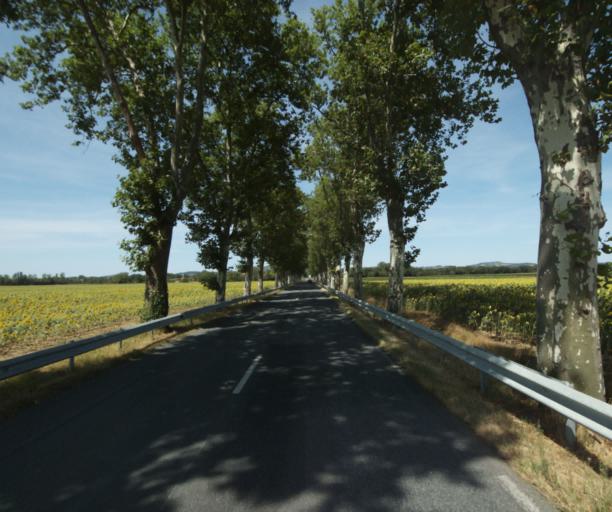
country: FR
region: Midi-Pyrenees
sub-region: Departement de la Haute-Garonne
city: Revel
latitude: 43.5079
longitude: 2.0110
